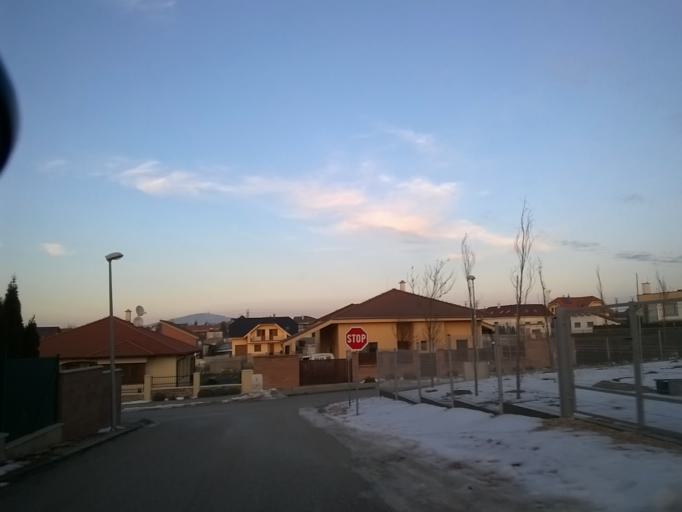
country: SK
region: Nitriansky
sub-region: Okres Nitra
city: Nitra
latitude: 48.2936
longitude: 18.0491
